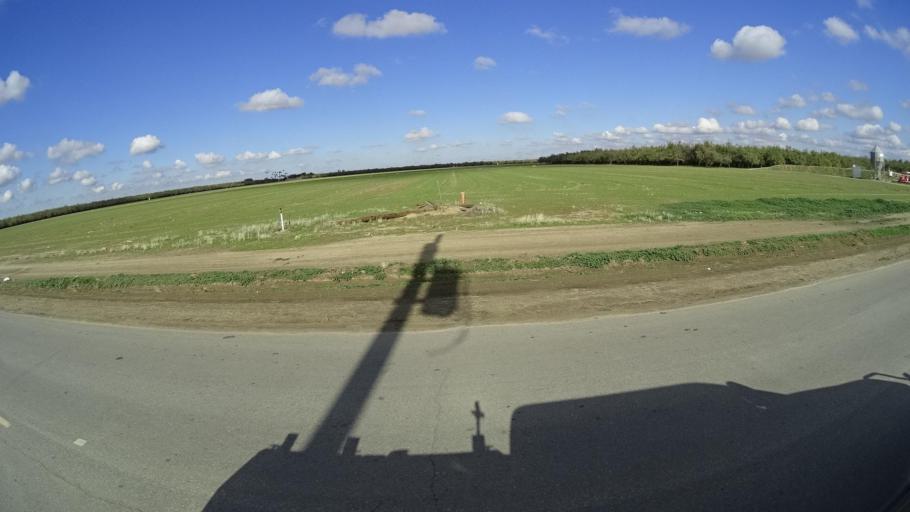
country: US
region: California
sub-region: Kern County
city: McFarland
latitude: 35.6741
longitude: -119.2643
